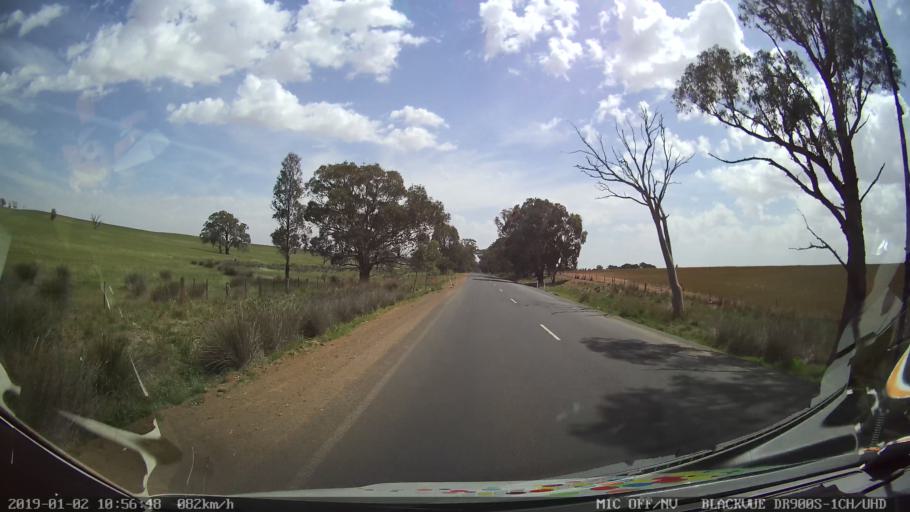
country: AU
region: New South Wales
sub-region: Cootamundra
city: Cootamundra
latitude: -34.6429
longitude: 148.2790
